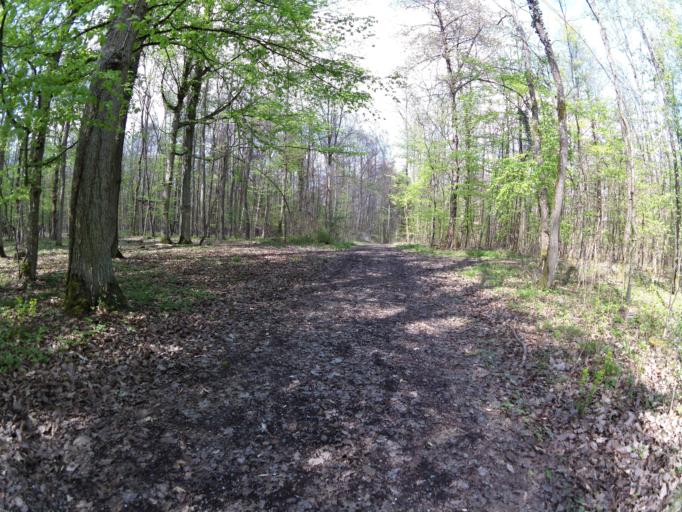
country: DE
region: Bavaria
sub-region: Regierungsbezirk Unterfranken
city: Greussenheim
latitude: 49.7901
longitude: 9.7792
